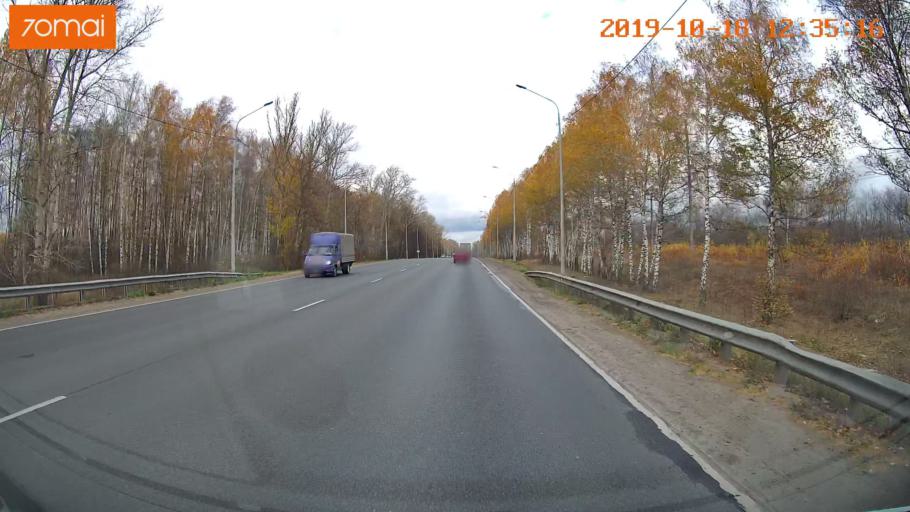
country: RU
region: Rjazan
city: Ryazan'
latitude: 54.6226
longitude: 39.6360
